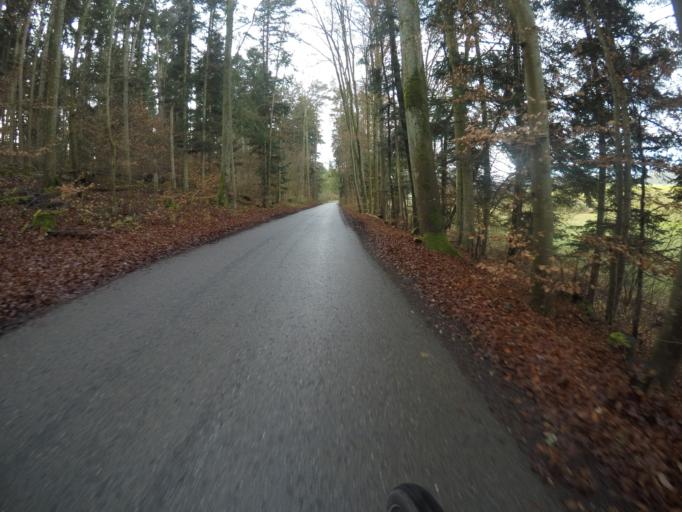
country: DE
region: Baden-Wuerttemberg
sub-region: Regierungsbezirk Stuttgart
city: Deckenpfronn
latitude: 48.6716
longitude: 8.8342
